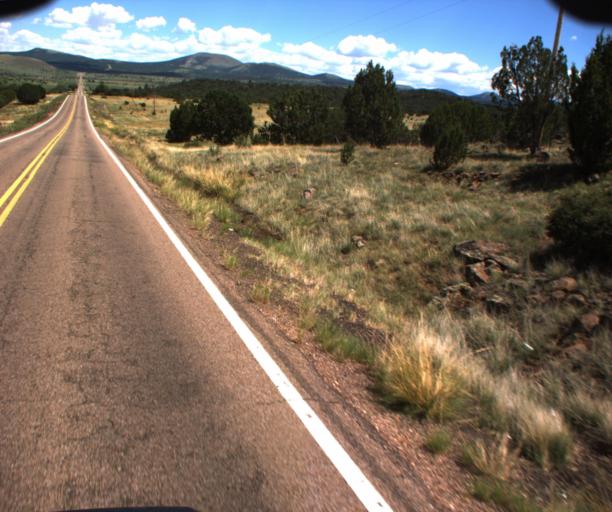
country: US
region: Arizona
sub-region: Navajo County
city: Pinetop-Lakeside
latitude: 34.2722
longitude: -109.6893
